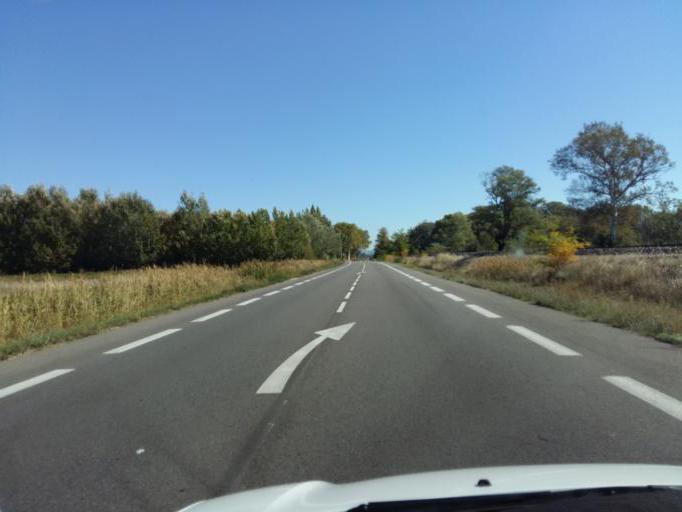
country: FR
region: Provence-Alpes-Cote d'Azur
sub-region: Departement des Bouches-du-Rhone
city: Charleval
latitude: 43.7541
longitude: 5.2419
